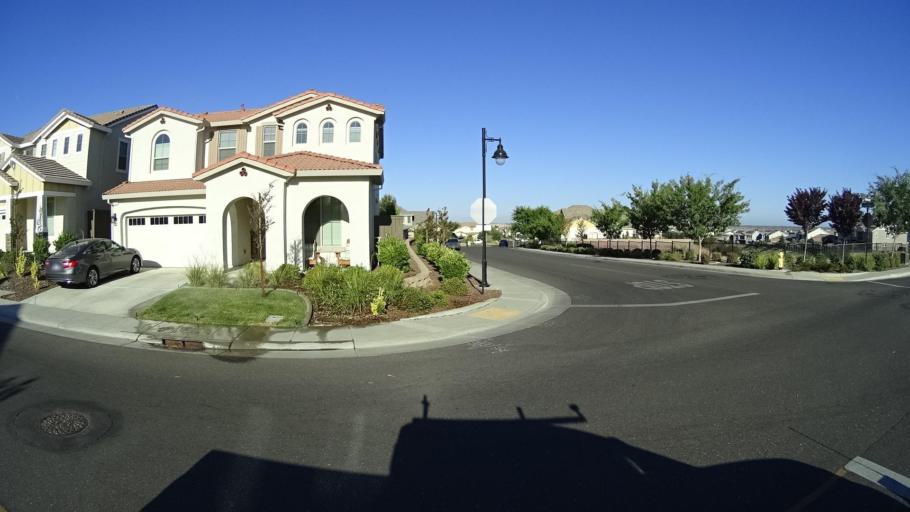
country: US
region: California
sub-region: Placer County
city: Rocklin
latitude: 38.8359
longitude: -121.2697
